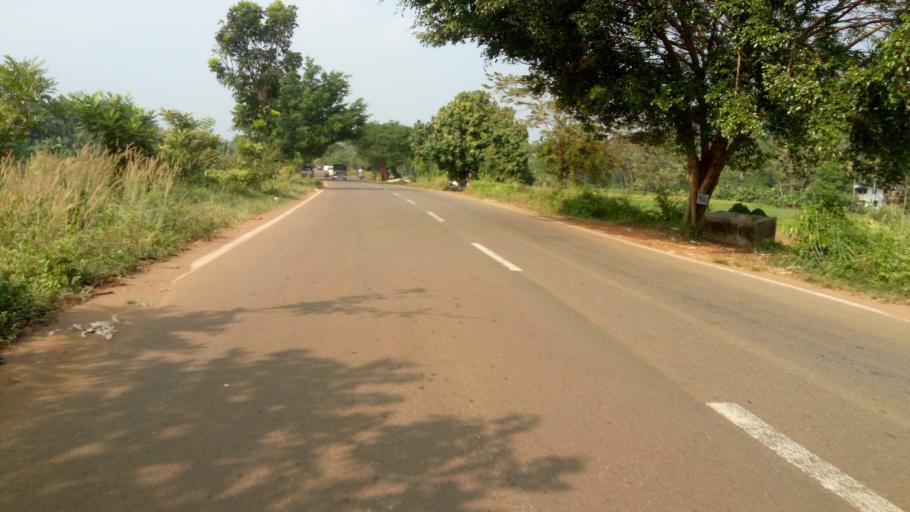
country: IN
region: Kerala
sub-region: Malappuram
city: Malappuram
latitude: 10.9991
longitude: 76.0150
